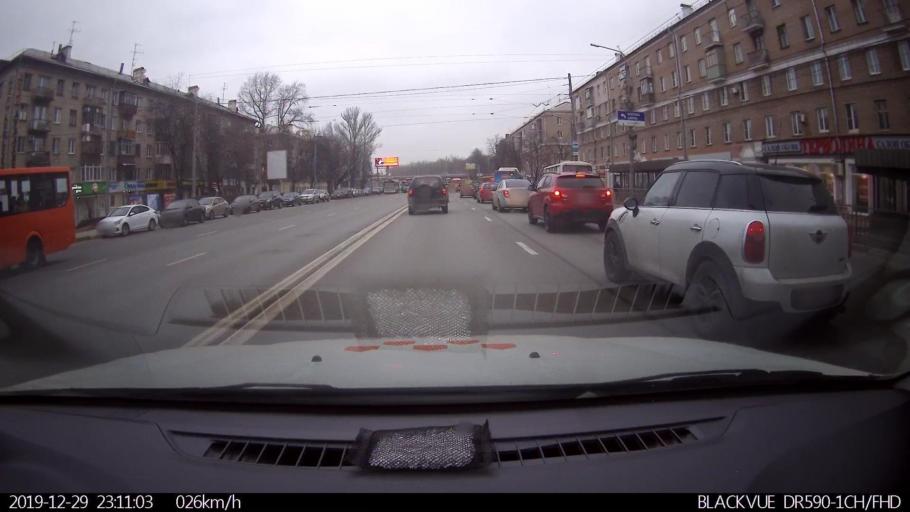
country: RU
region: Nizjnij Novgorod
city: Nizhniy Novgorod
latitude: 56.2657
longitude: 43.9126
